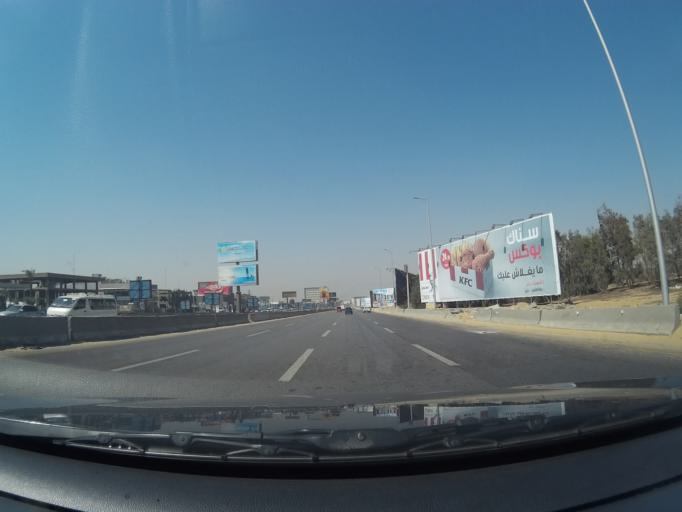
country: EG
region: Muhafazat al Qahirah
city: Cairo
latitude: 30.0009
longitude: 31.3955
